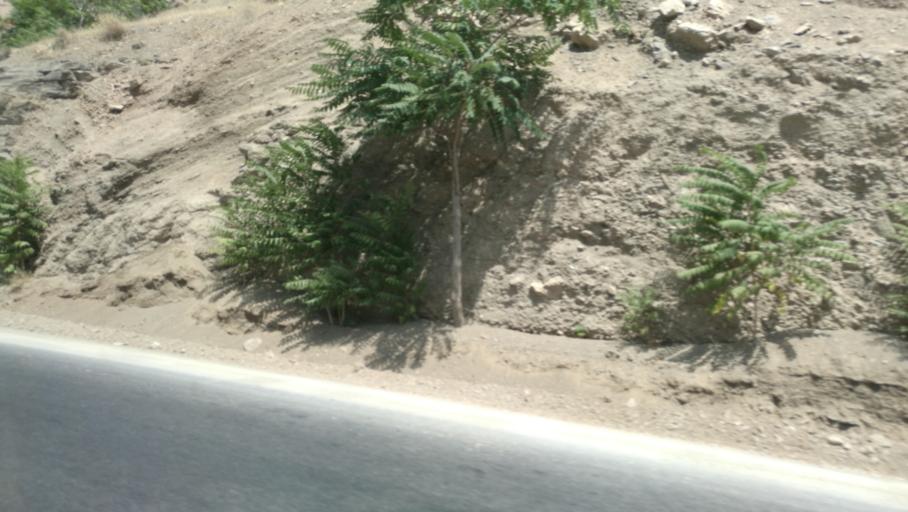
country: IR
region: Alborz
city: Karaj
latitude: 35.9277
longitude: 51.0606
